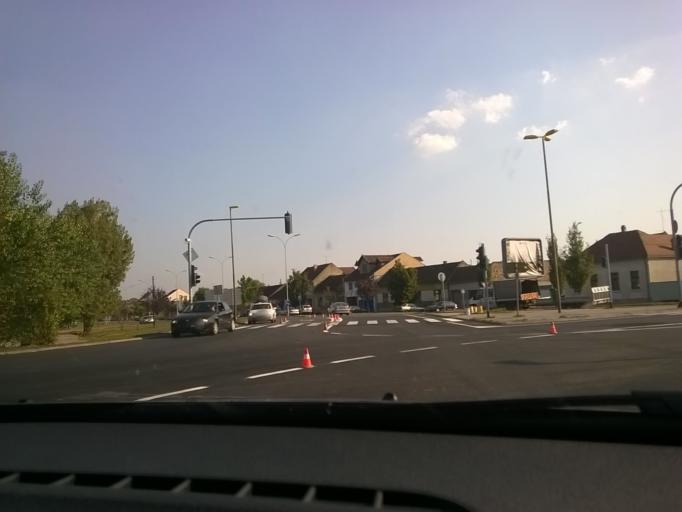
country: RS
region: Autonomna Pokrajina Vojvodina
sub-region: Juznobanatski Okrug
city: Vrsac
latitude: 45.1278
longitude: 21.2887
